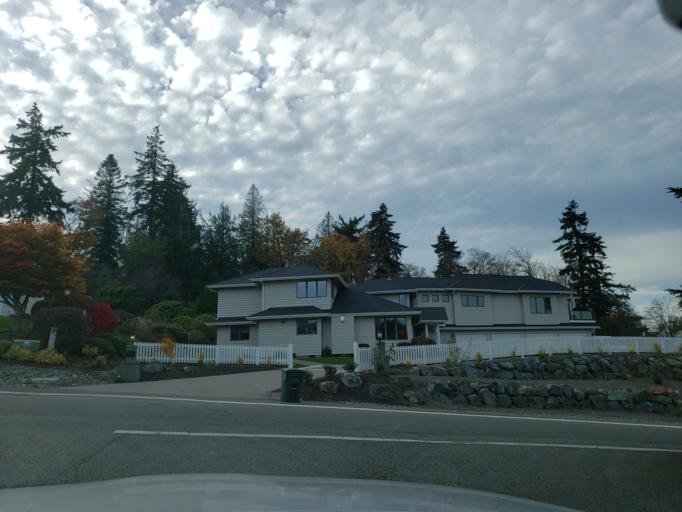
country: US
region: Washington
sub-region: Snohomish County
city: Woodway
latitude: 47.8023
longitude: -122.3870
